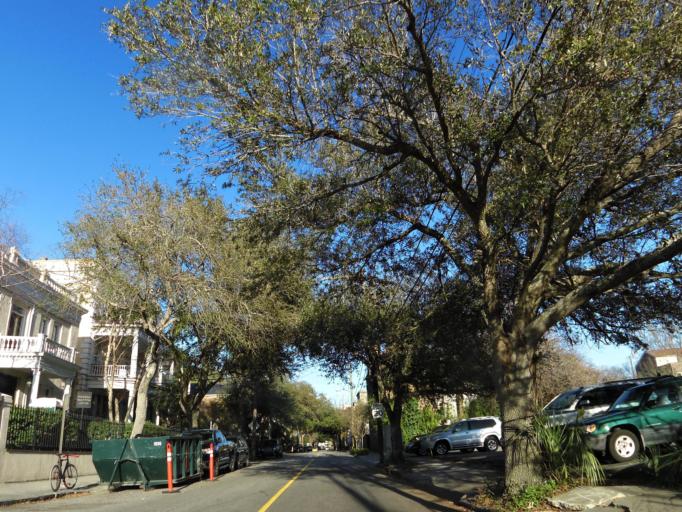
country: US
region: South Carolina
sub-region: Charleston County
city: Charleston
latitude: 32.7826
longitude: -79.9316
